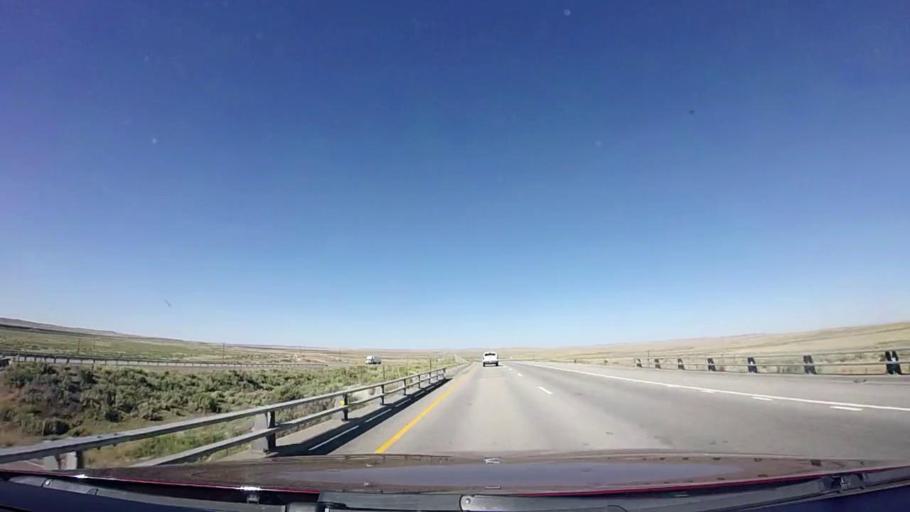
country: US
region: Wyoming
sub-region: Carbon County
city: Rawlins
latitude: 41.7854
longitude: -107.4109
